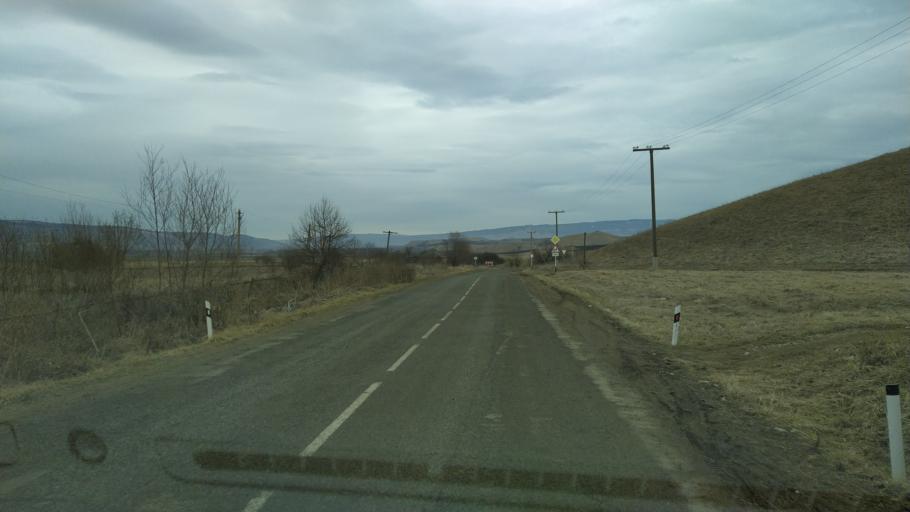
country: RU
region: Krasnodarskiy
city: Peredovaya
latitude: 44.0883
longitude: 41.3699
